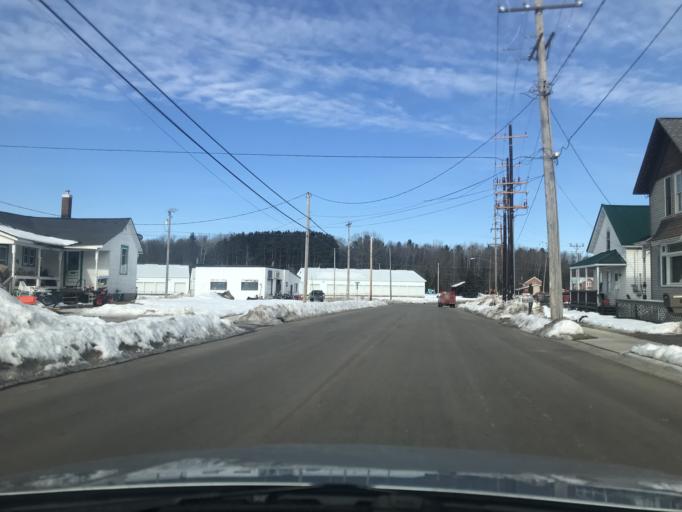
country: US
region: Wisconsin
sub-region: Oconto County
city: Gillett
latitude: 44.8911
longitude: -88.3024
